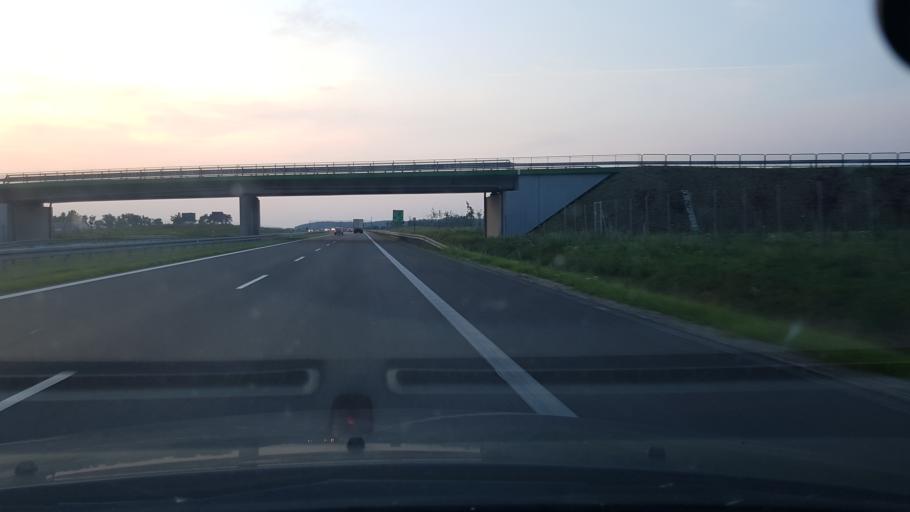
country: PL
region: Warmian-Masurian Voivodeship
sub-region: Powiat nidzicki
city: Nidzica
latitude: 53.3895
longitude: 20.3688
